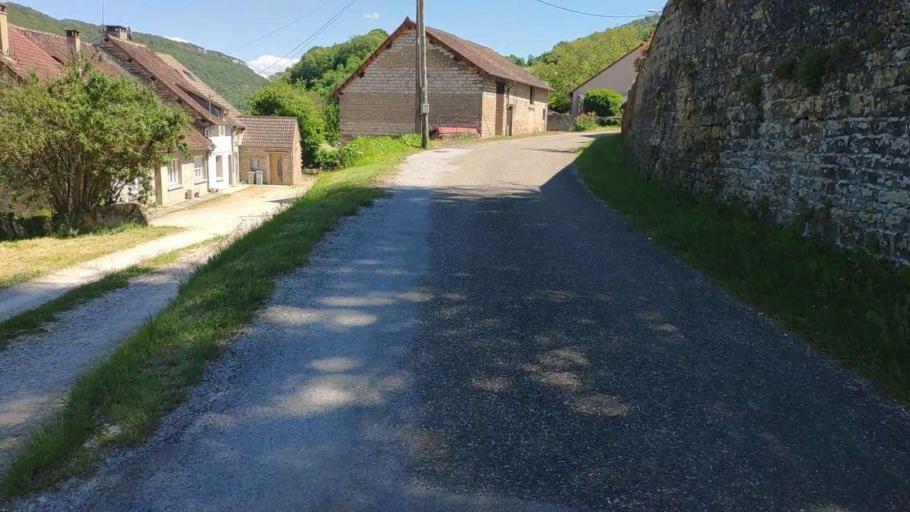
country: FR
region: Franche-Comte
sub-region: Departement du Jura
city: Perrigny
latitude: 46.7508
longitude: 5.6137
